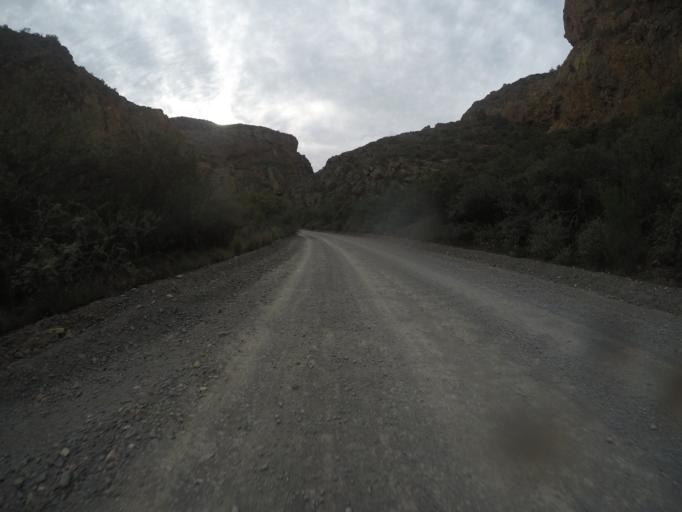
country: ZA
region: Eastern Cape
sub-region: Cacadu District Municipality
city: Willowmore
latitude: -33.5225
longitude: 23.6529
